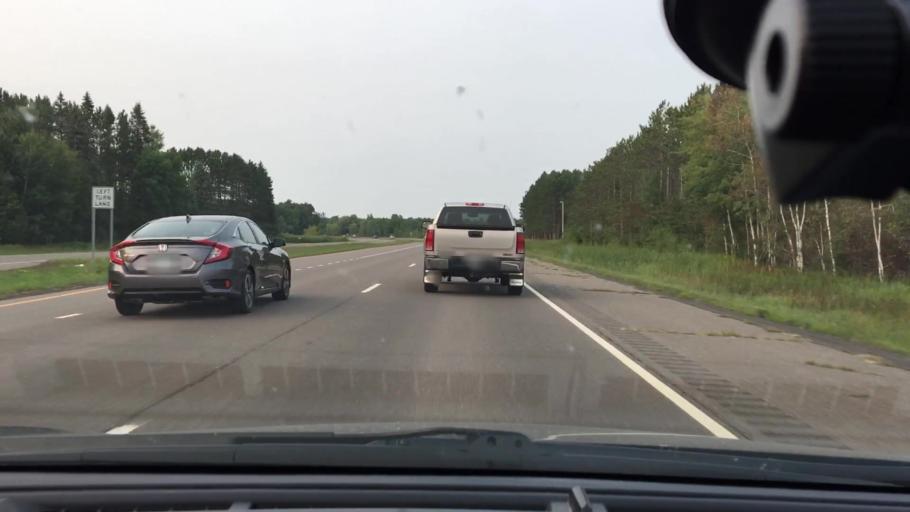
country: US
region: Minnesota
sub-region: Mille Lacs County
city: Vineland
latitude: 46.0884
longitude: -93.6461
